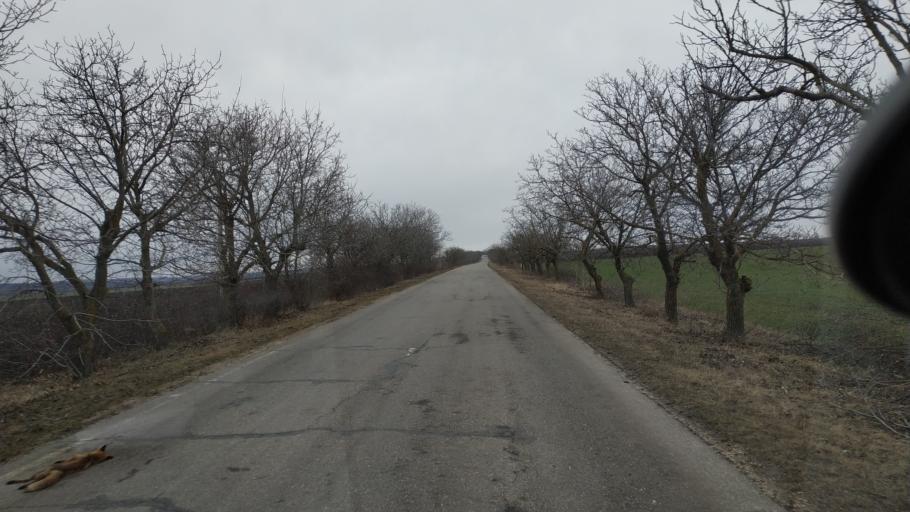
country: MD
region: Telenesti
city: Cocieri
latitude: 47.3472
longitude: 29.0474
